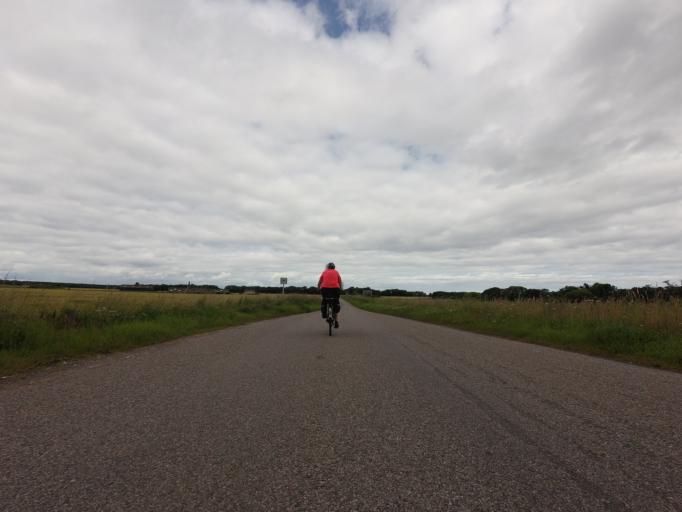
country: GB
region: Scotland
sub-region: Moray
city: Forres
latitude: 57.6229
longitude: -3.6511
